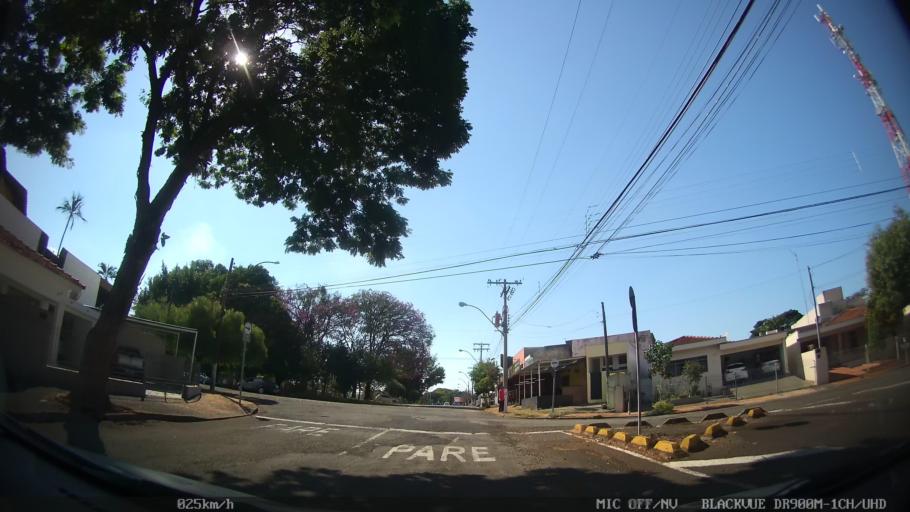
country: BR
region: Sao Paulo
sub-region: Americana
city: Americana
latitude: -22.7331
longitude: -47.3206
